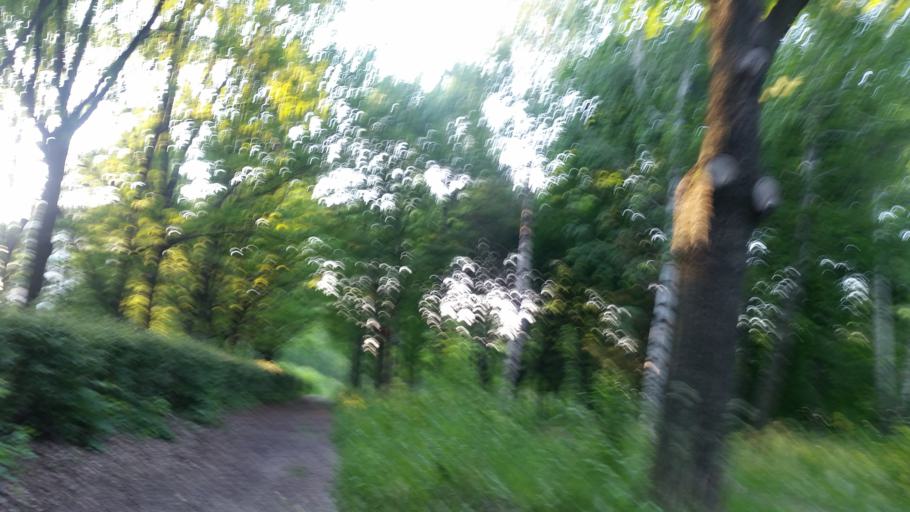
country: RU
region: Ulyanovsk
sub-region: Ulyanovskiy Rayon
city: Ulyanovsk
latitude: 54.3448
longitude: 48.3970
